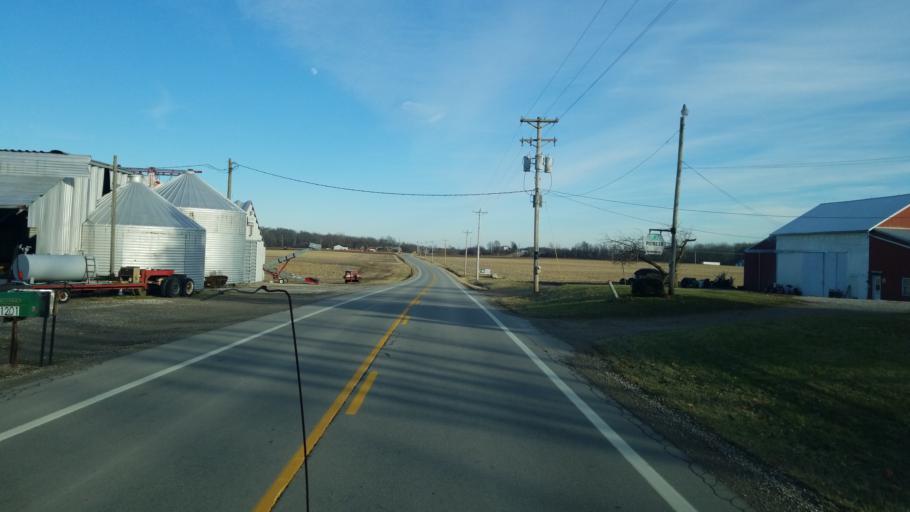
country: US
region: Ohio
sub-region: Huron County
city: Greenwich
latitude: 41.1029
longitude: -82.5441
